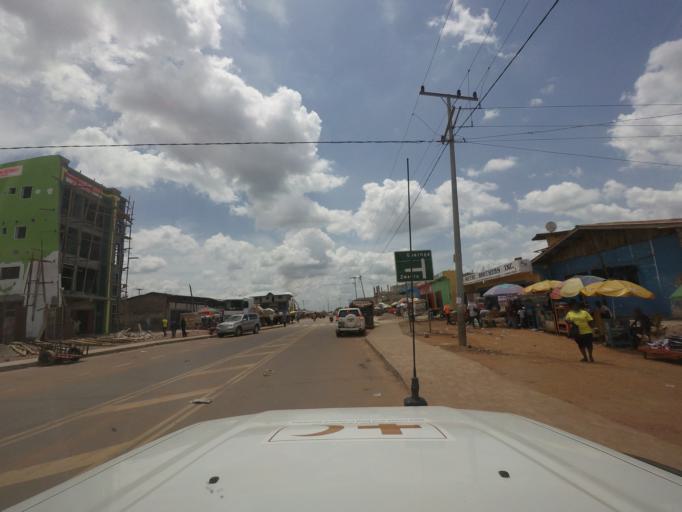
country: LR
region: Nimba
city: Sanniquellie
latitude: 7.2336
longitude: -8.9854
